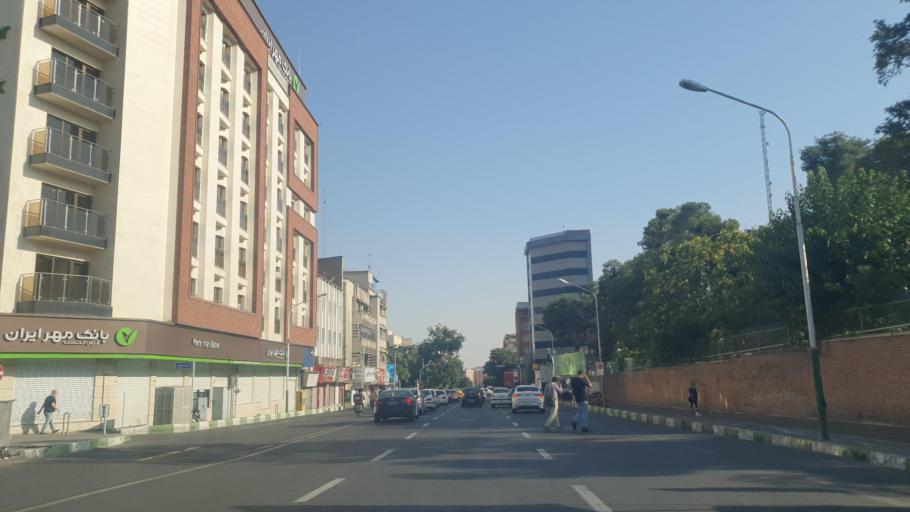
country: IR
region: Tehran
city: Tehran
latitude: 35.7082
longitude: 51.4256
